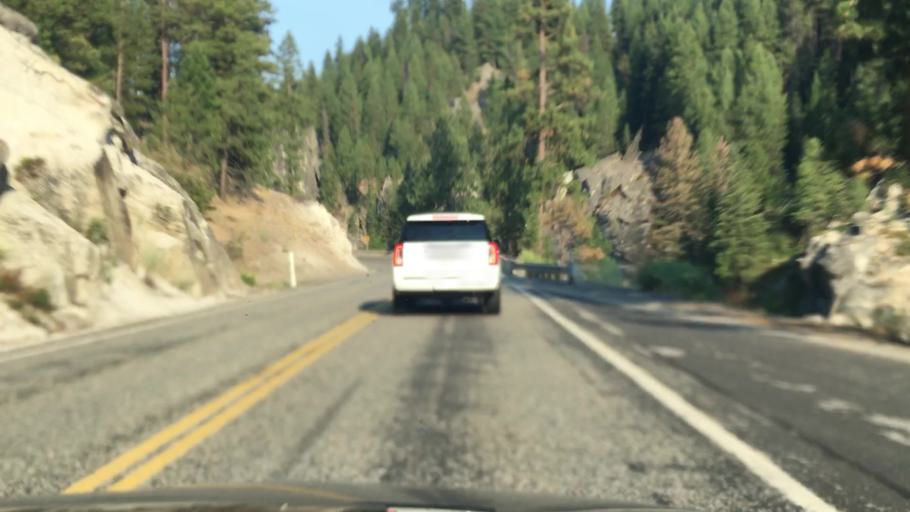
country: US
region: Idaho
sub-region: Valley County
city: Cascade
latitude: 44.3124
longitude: -116.0789
